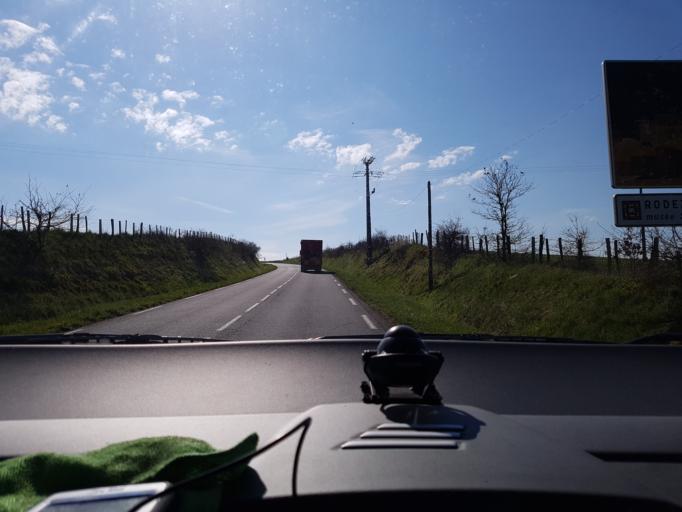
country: FR
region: Midi-Pyrenees
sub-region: Departement de l'Aveyron
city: Moyrazes
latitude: 44.3730
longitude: 2.4616
